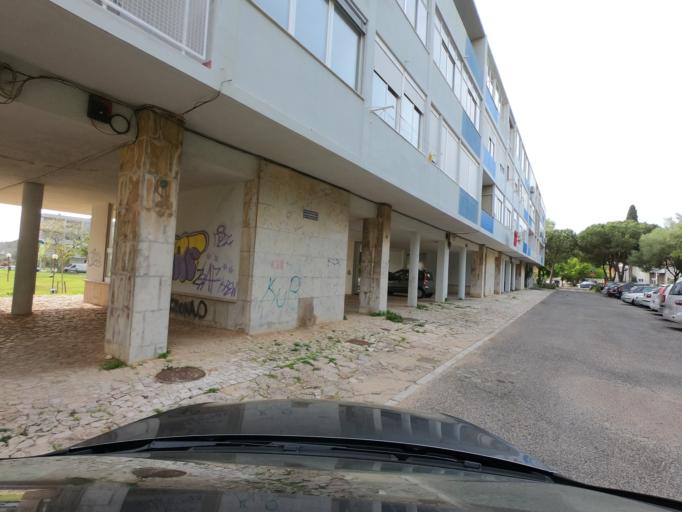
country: PT
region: Lisbon
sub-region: Oeiras
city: Carcavelos
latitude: 38.6909
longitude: -9.3223
